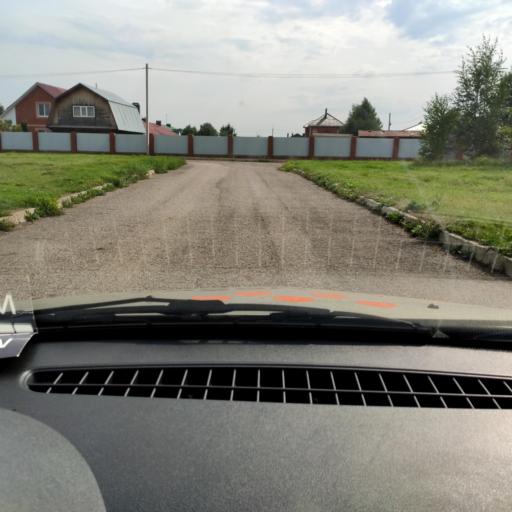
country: RU
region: Bashkortostan
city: Ufa
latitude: 54.8281
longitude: 55.9989
